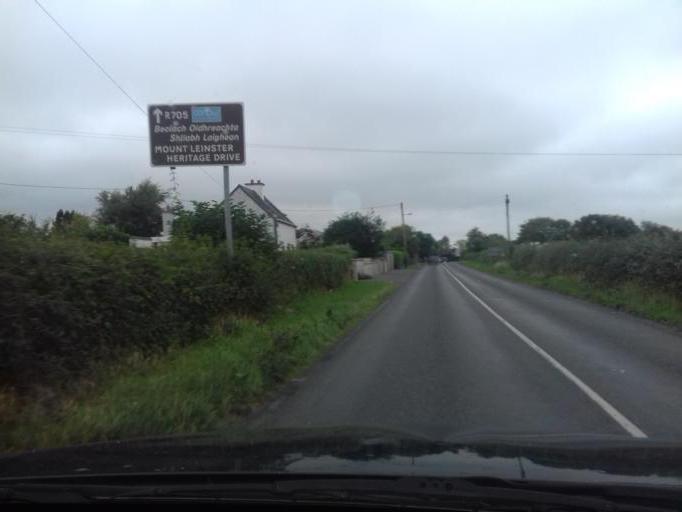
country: IE
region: Leinster
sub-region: County Carlow
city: Bagenalstown
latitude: 52.6912
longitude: -6.9614
